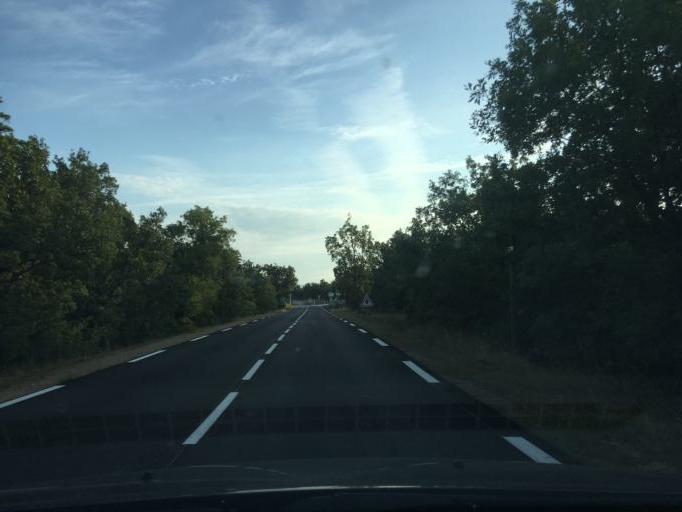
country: FR
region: Provence-Alpes-Cote d'Azur
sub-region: Departement du Var
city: Aups
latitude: 43.7196
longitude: 6.2231
